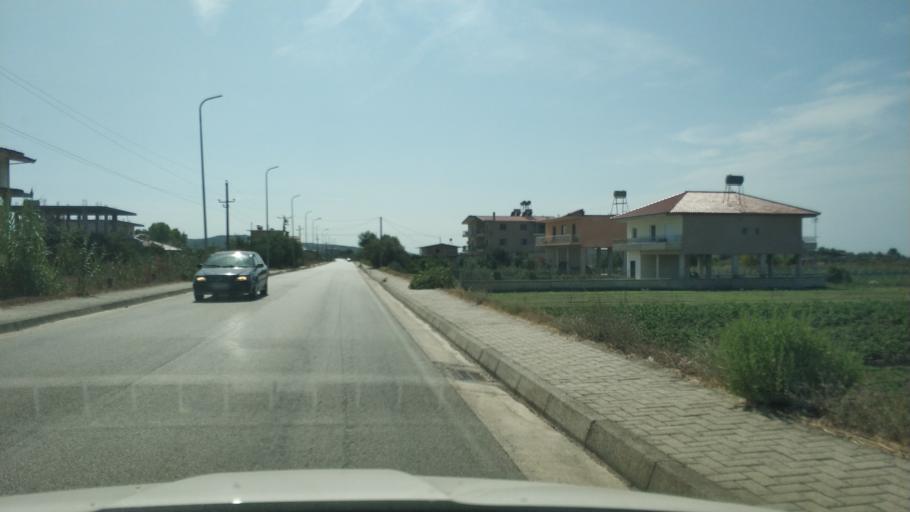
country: AL
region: Fier
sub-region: Rrethi i Lushnjes
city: Divjake
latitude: 40.9844
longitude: 19.5344
